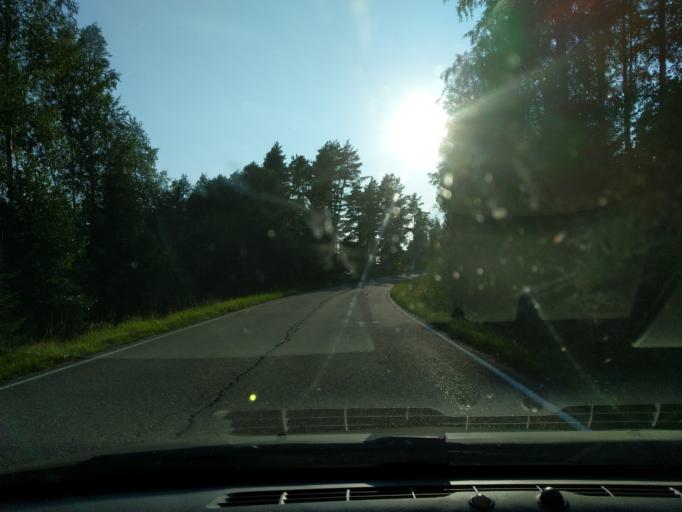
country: FI
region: Uusimaa
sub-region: Helsinki
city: Vihti
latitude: 60.5311
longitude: 24.3535
